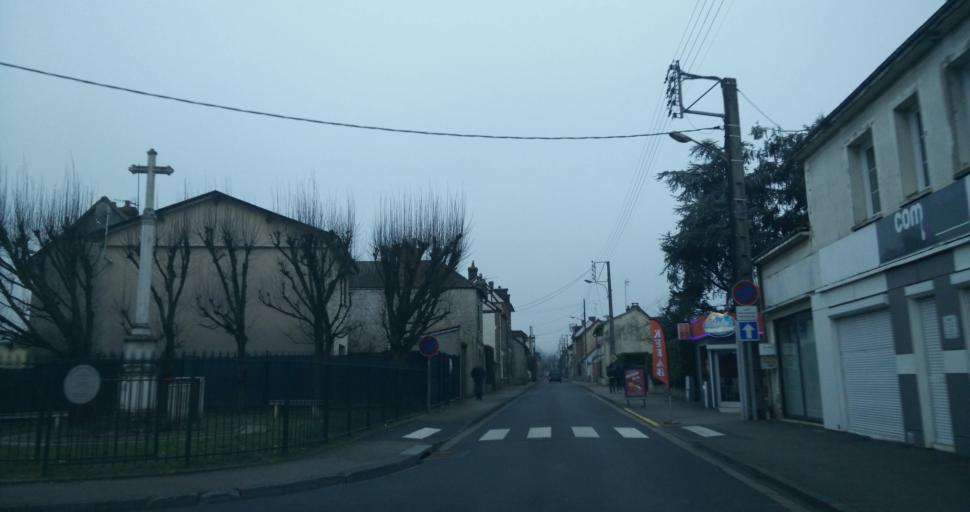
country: FR
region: Haute-Normandie
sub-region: Departement de l'Eure
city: Louviers
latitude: 49.2097
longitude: 1.1626
